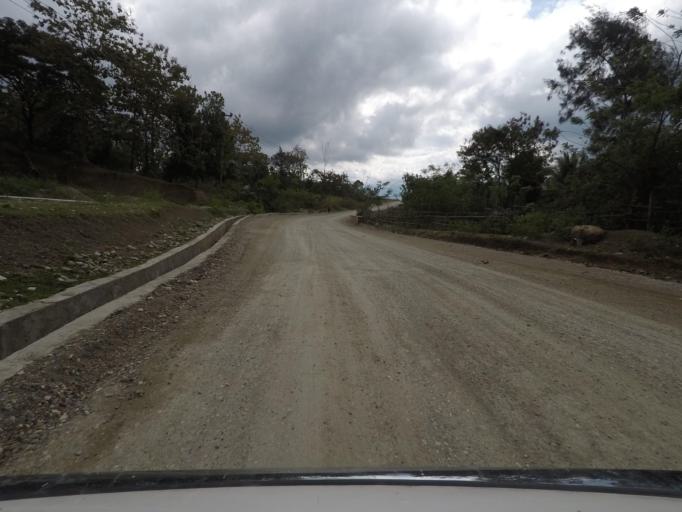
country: TL
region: Viqueque
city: Viqueque
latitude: -8.8021
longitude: 126.3785
